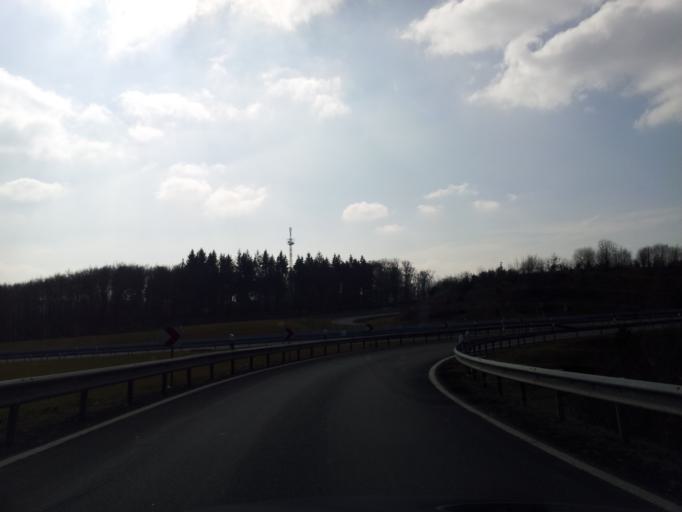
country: DE
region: Rheinland-Pfalz
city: Altrich
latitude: 49.9487
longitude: 6.8850
